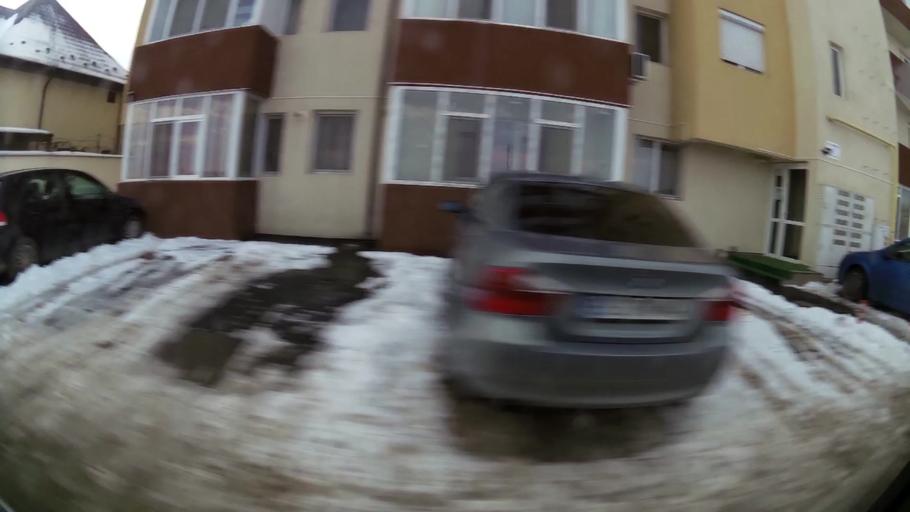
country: RO
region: Ilfov
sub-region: Comuna Popesti-Leordeni
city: Popesti-Leordeni
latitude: 44.3644
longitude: 26.1524
